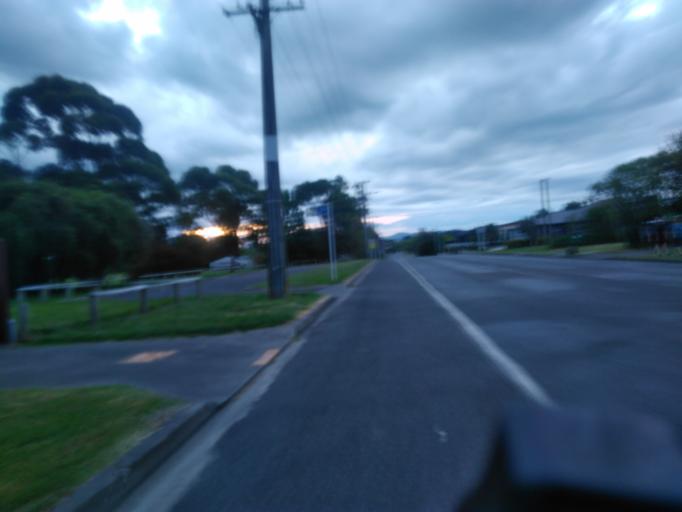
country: NZ
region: Gisborne
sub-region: Gisborne District
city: Gisborne
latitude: -38.6444
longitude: 177.9974
